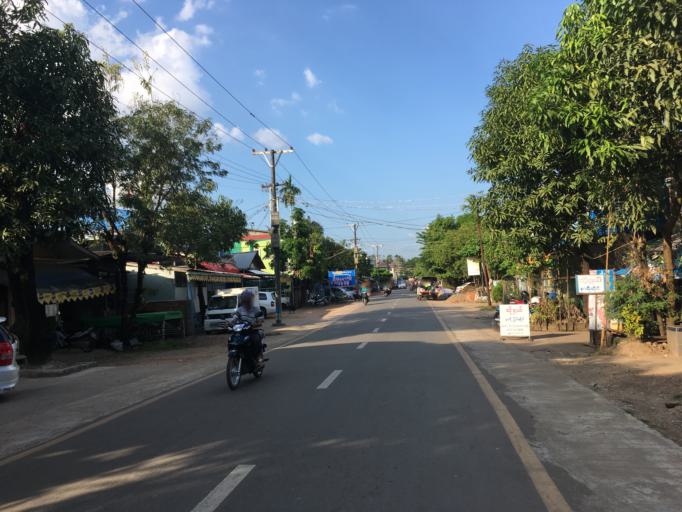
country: MM
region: Mon
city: Mawlamyine
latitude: 16.4539
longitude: 97.6256
